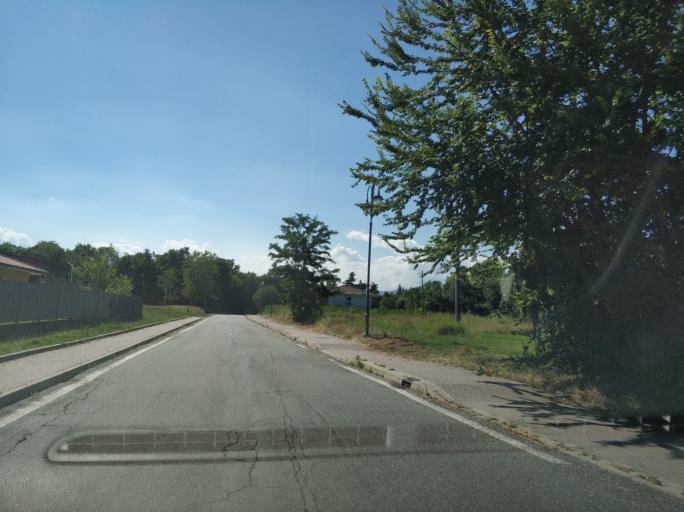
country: IT
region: Piedmont
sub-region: Provincia di Torino
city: Lombardore
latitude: 45.2378
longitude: 7.7305
